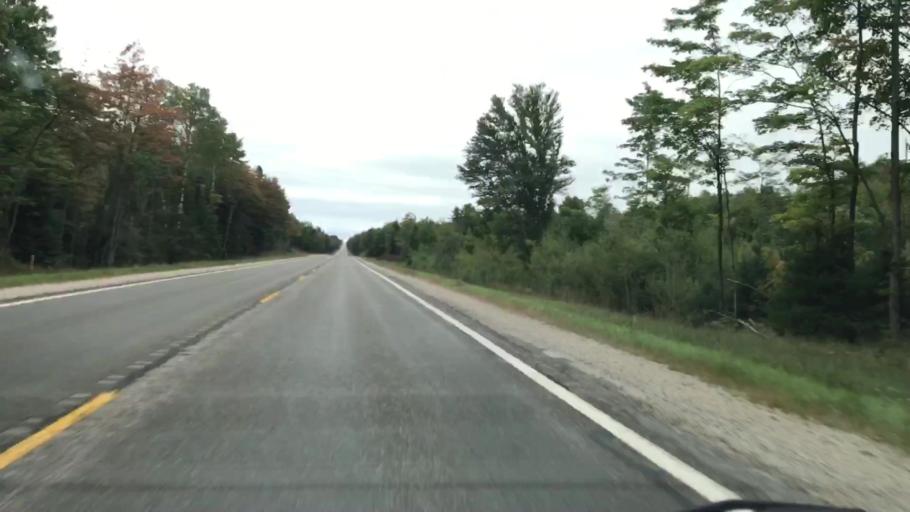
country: US
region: Michigan
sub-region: Luce County
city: Newberry
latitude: 46.2407
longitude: -85.5723
